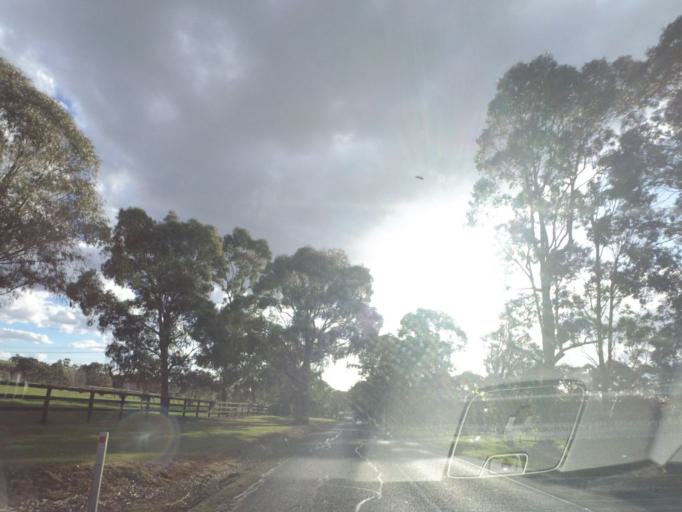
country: AU
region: Victoria
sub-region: Yarra Ranges
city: Chirnside Park
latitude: -37.7156
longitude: 145.3321
